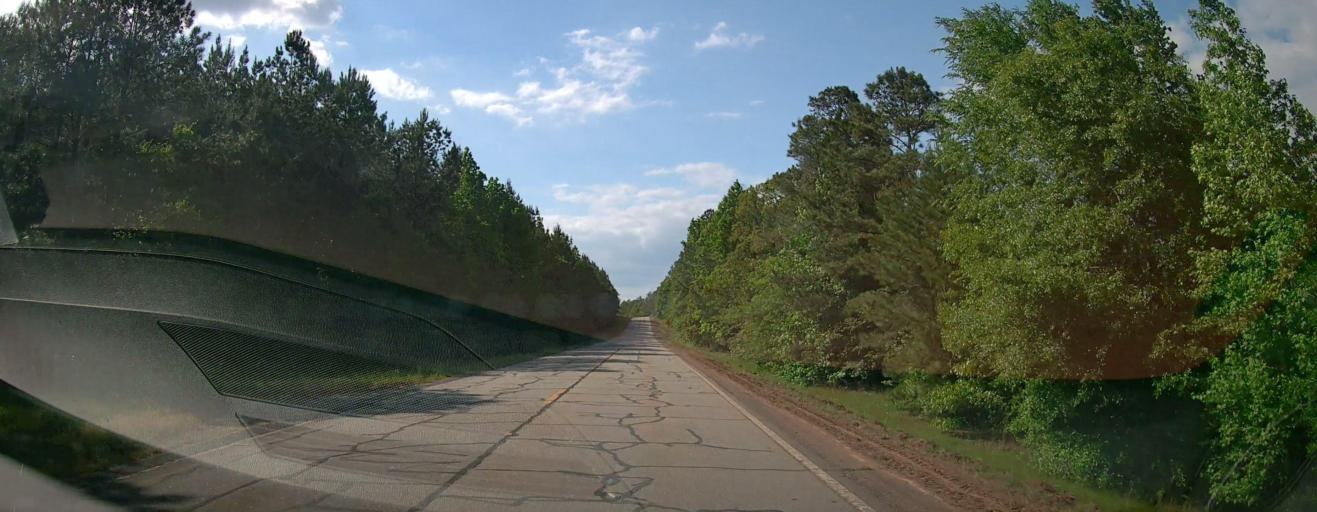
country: US
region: Georgia
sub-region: Washington County
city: Tennille
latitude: 32.9226
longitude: -83.0023
